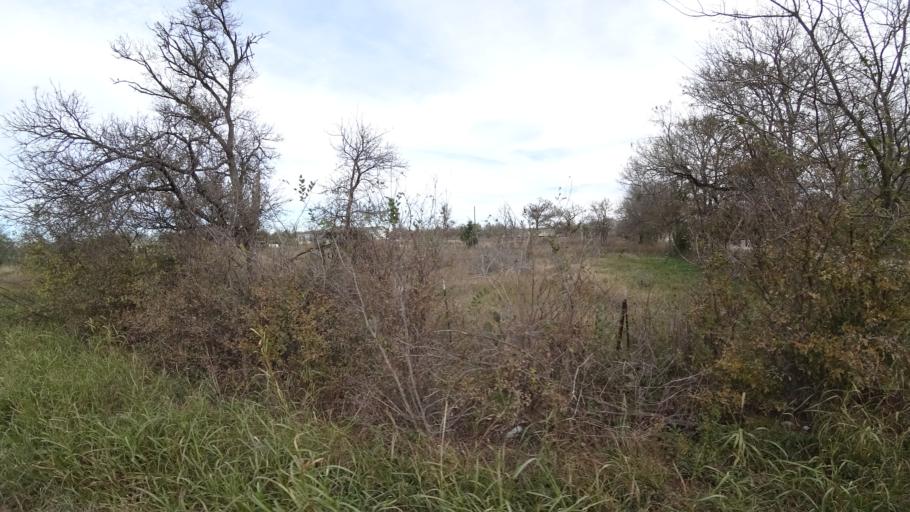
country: US
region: Texas
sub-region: Travis County
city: Garfield
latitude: 30.1085
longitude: -97.5743
